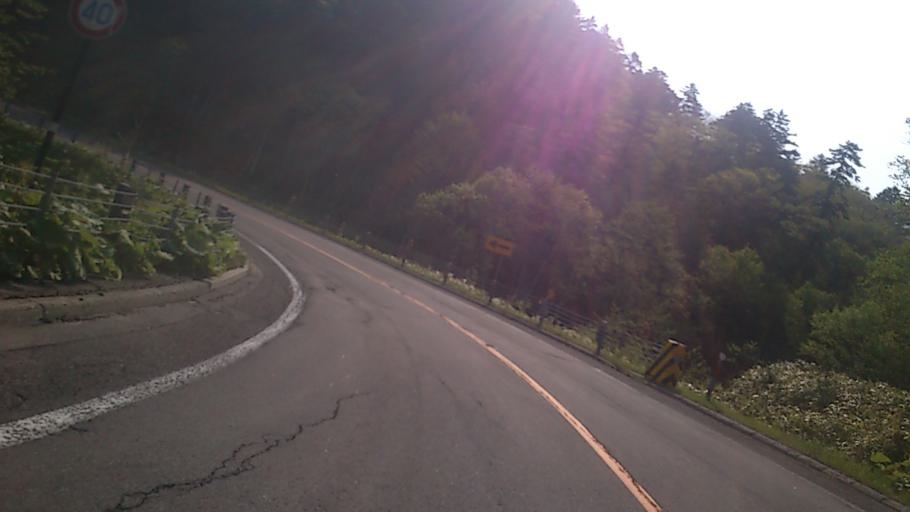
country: JP
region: Hokkaido
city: Bihoro
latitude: 43.4507
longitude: 144.2268
